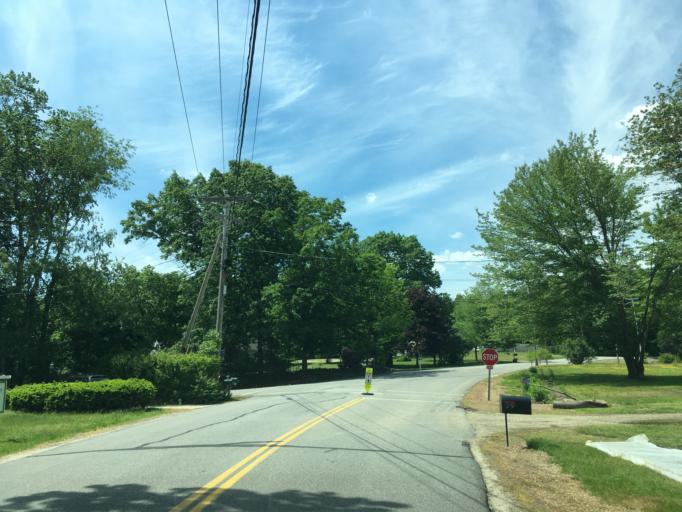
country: US
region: New Hampshire
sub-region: Rockingham County
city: Stratham Station
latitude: 43.0341
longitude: -70.8803
